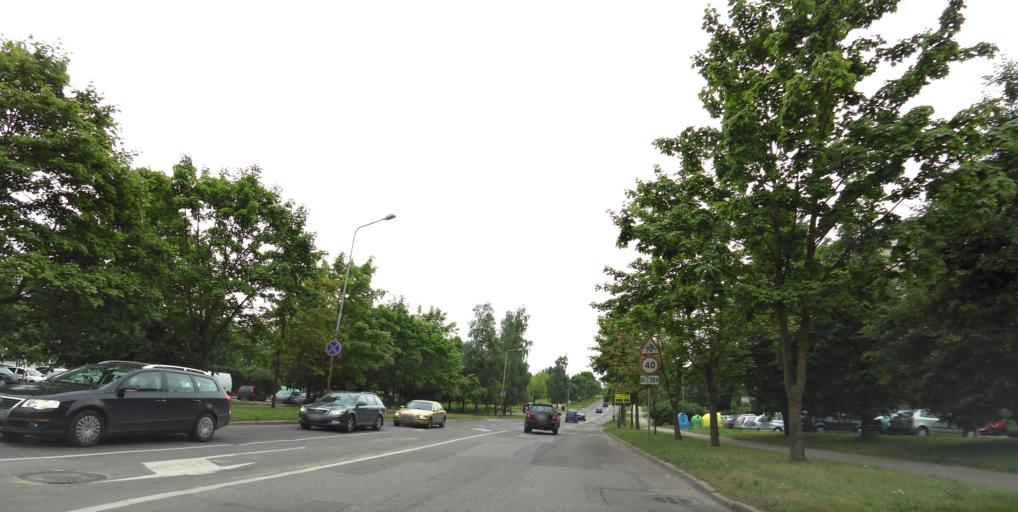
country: LT
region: Vilnius County
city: Seskine
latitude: 54.7162
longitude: 25.2576
